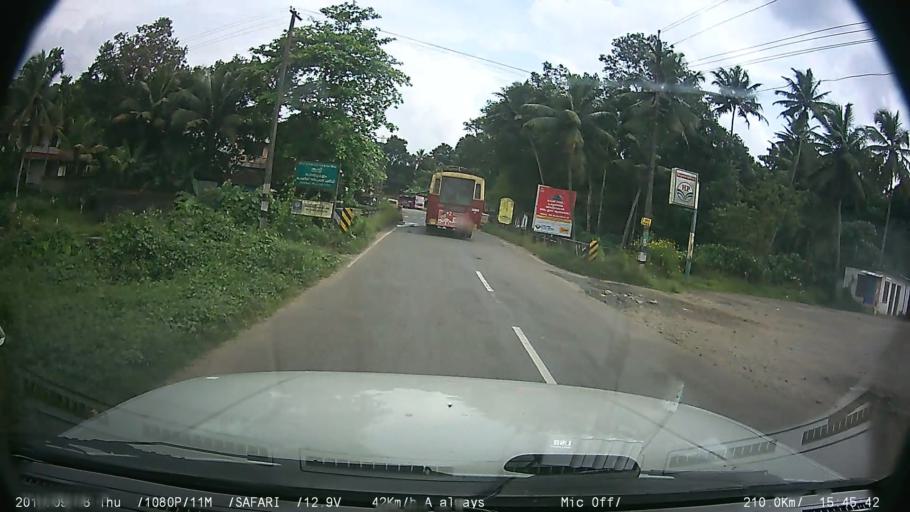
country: IN
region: Kerala
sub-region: Ernakulam
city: Piravam
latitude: 9.8422
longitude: 76.5918
